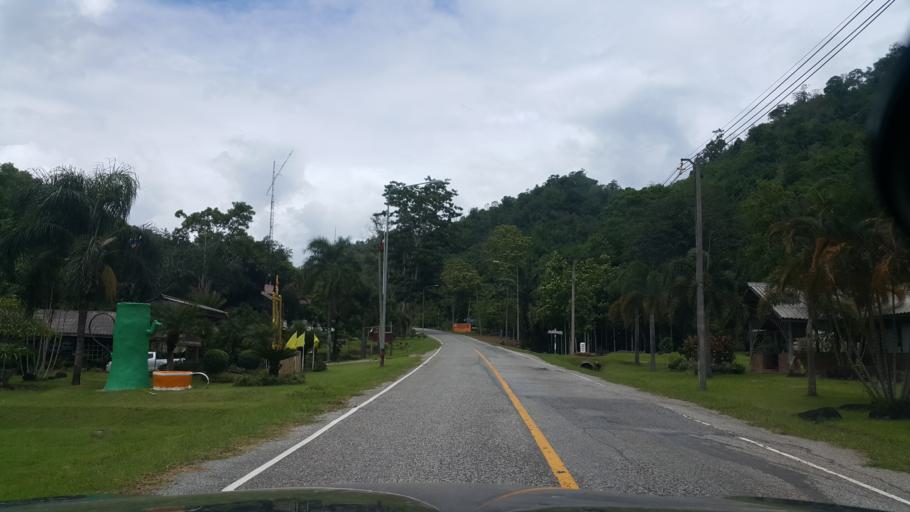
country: TH
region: Loei
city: Na Haeo
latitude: 17.6332
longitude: 100.8975
